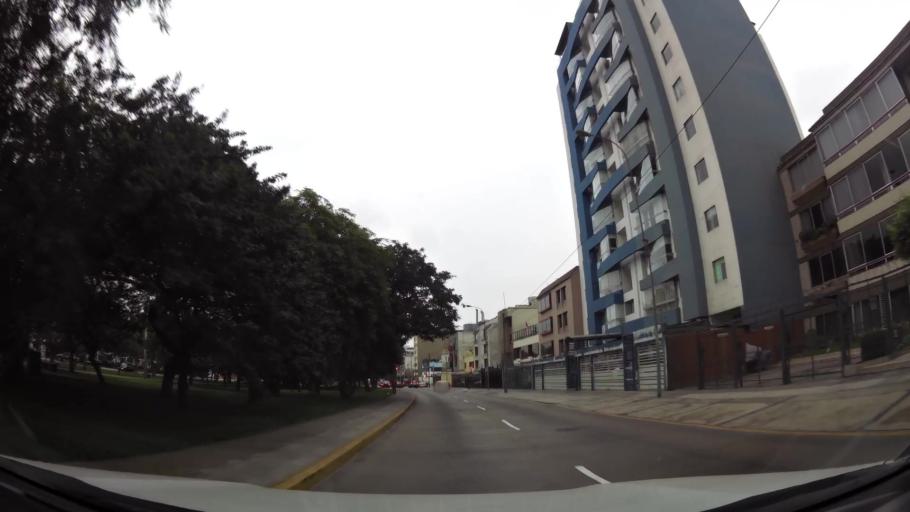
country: PE
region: Lima
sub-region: Lima
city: San Luis
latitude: -12.0939
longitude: -77.0048
